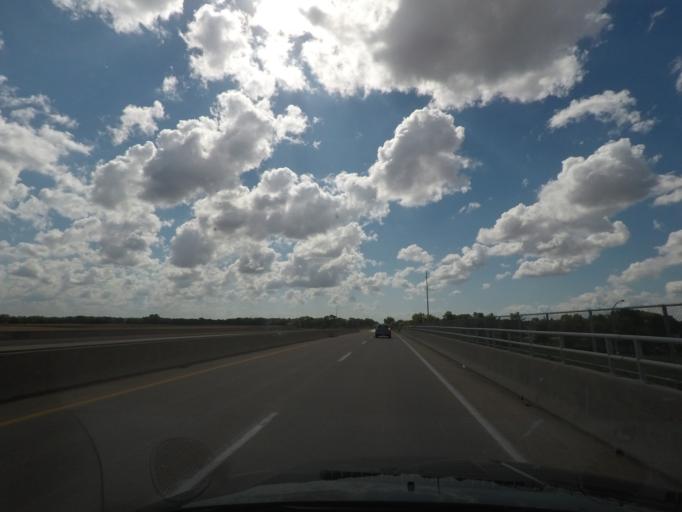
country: US
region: Iowa
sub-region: Story County
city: Ames
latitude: 42.0088
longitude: -93.6787
